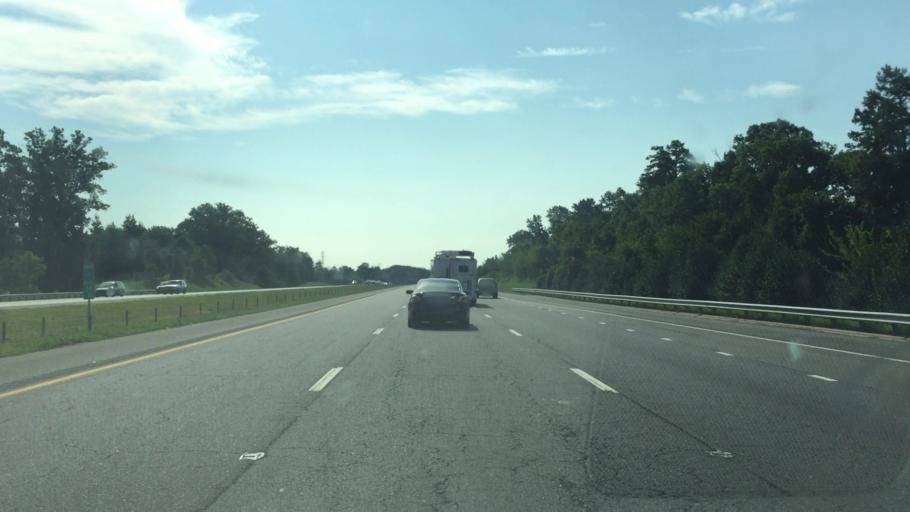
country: US
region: North Carolina
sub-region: Cabarrus County
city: Harrisburg
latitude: 35.3078
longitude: -80.6984
